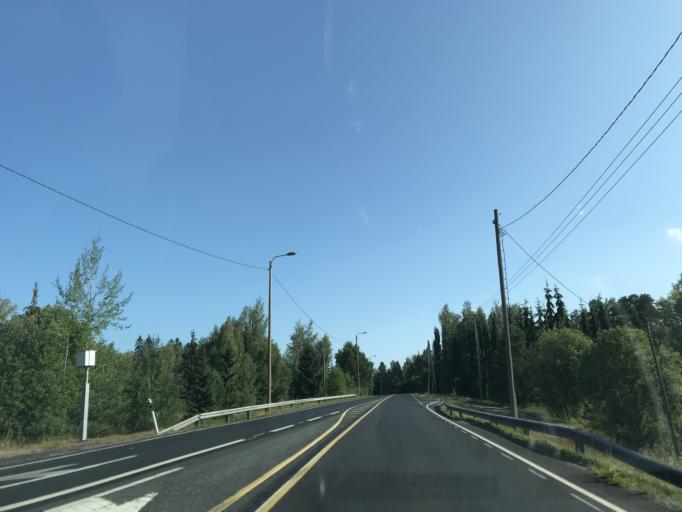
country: FI
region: Paijanne Tavastia
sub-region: Lahti
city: Lahti
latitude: 61.0512
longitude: 25.6679
